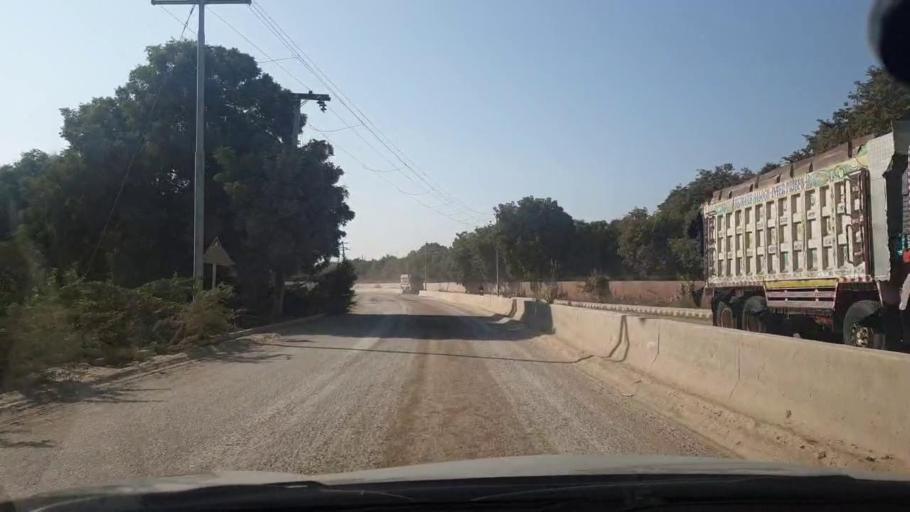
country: PK
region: Sindh
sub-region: Karachi District
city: Karachi
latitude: 25.0876
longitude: 67.0126
